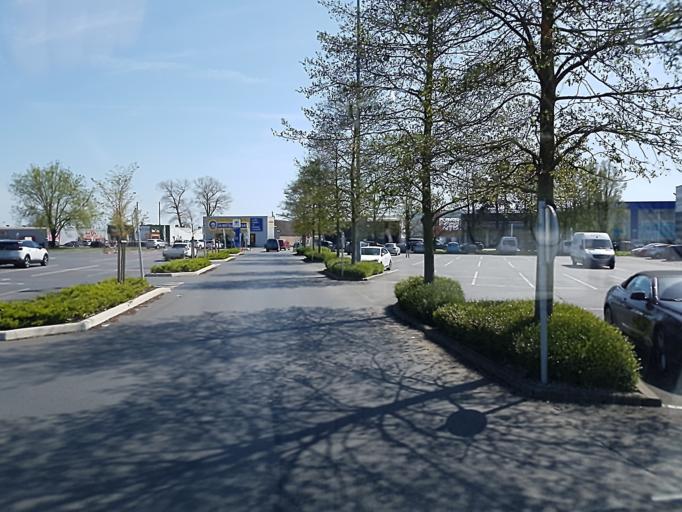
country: BE
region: Wallonia
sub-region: Province du Hainaut
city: Tournai
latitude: 50.6251
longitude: 3.3691
